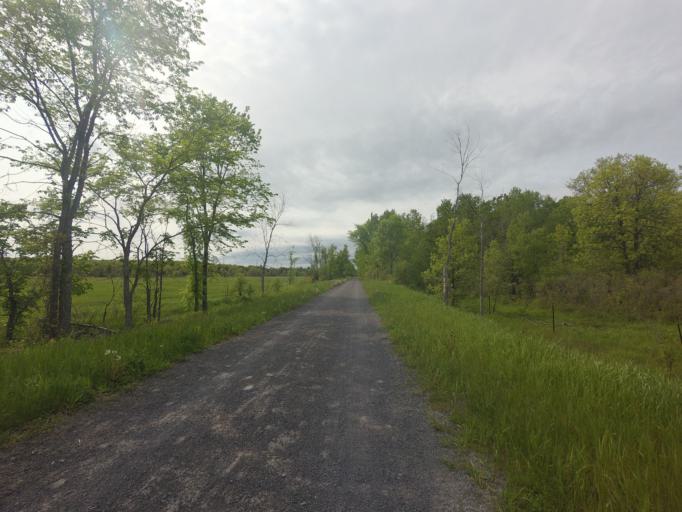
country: CA
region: Ontario
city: Kingston
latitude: 44.3500
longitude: -76.6133
